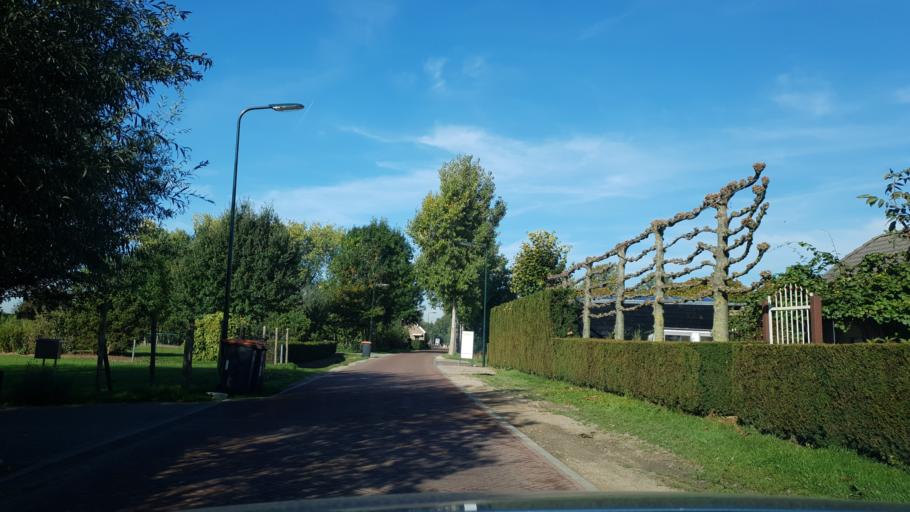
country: NL
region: Gelderland
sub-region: Gemeente Beuningen
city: Beuningen
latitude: 51.8632
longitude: 5.7328
